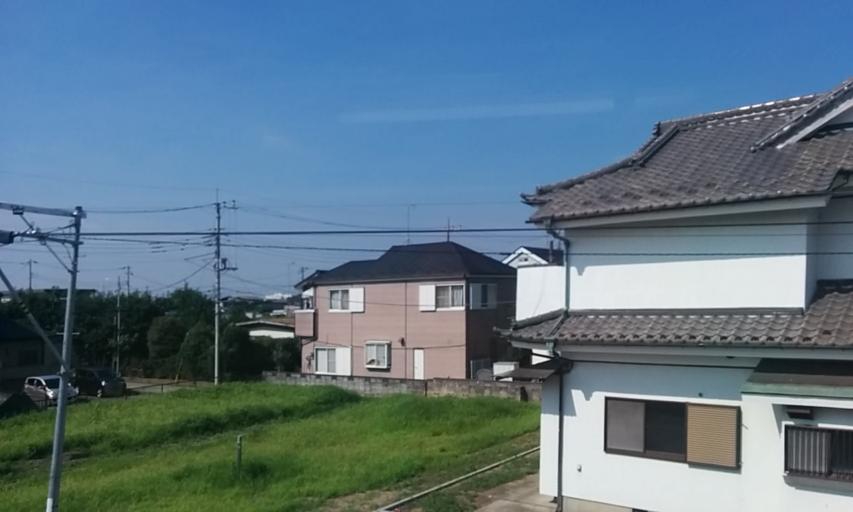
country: JP
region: Saitama
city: Kukichuo
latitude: 36.0812
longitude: 139.6765
